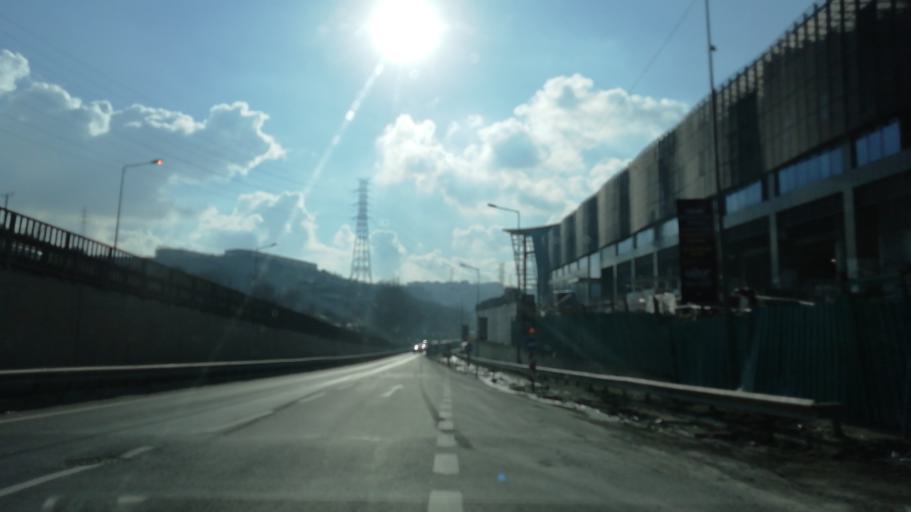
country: TR
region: Istanbul
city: Sisli
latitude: 41.0928
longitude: 28.9533
